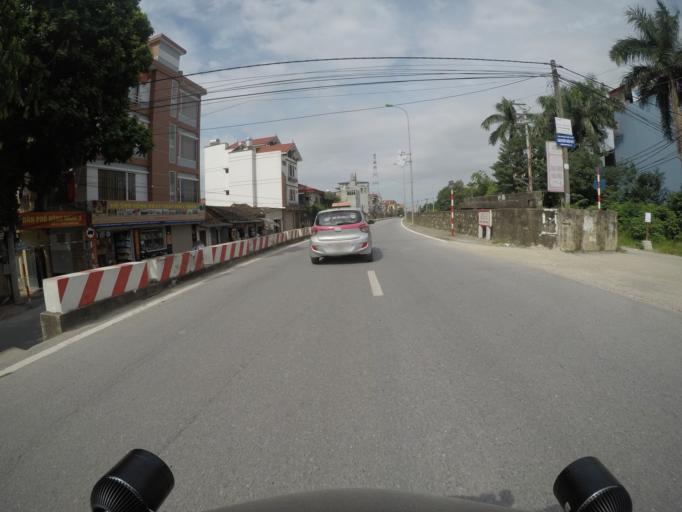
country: VN
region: Ha Noi
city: Tay Ho
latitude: 21.0920
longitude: 105.7829
